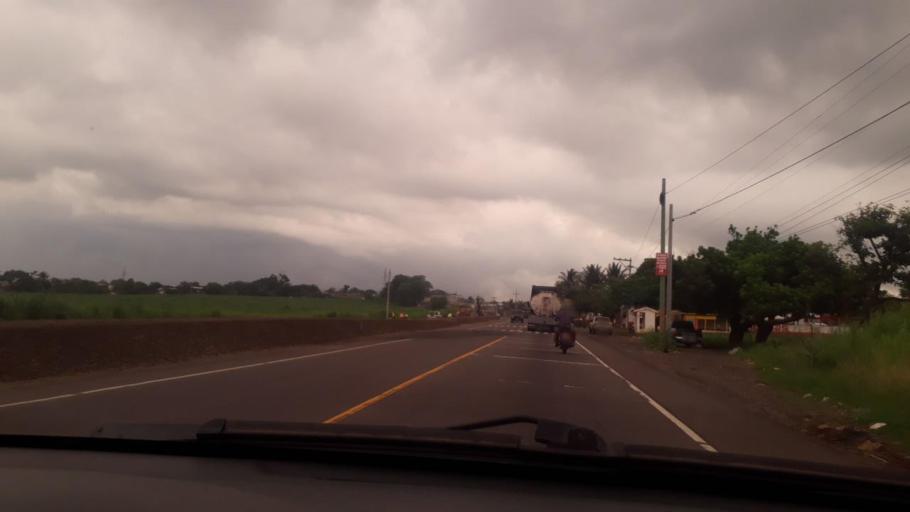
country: GT
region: Escuintla
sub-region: Municipio de Escuintla
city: Escuintla
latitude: 14.2743
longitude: -90.7590
